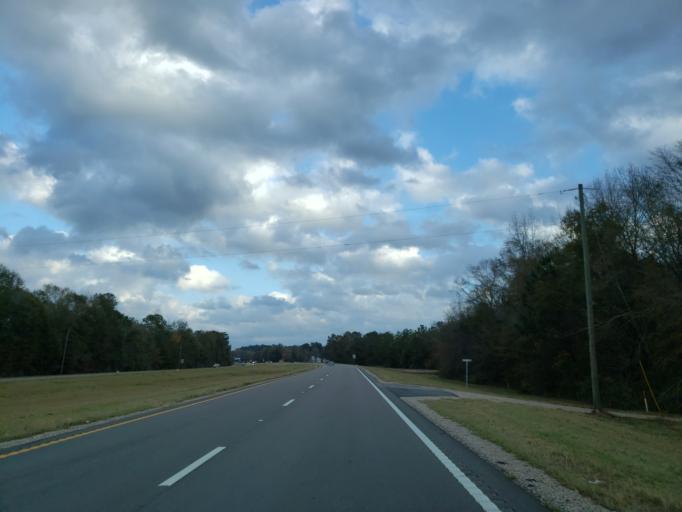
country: US
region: Mississippi
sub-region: Perry County
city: New Augusta
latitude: 31.2016
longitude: -89.0486
